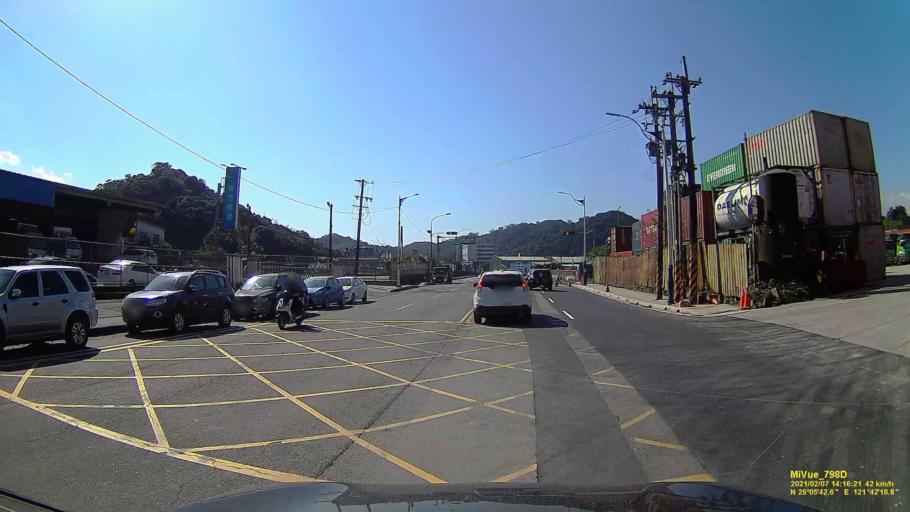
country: TW
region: Taiwan
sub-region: Keelung
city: Keelung
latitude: 25.0952
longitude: 121.7051
